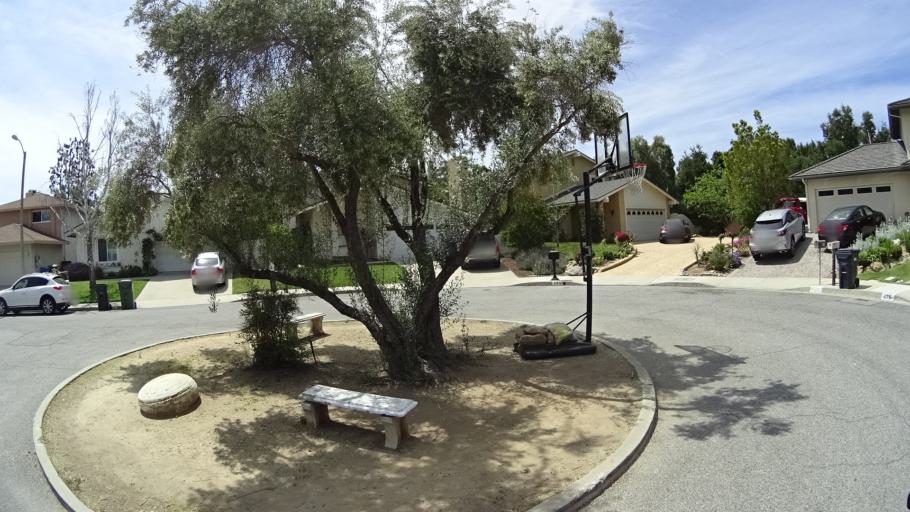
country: US
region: California
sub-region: Ventura County
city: Casa Conejo
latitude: 34.1943
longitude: -118.8888
